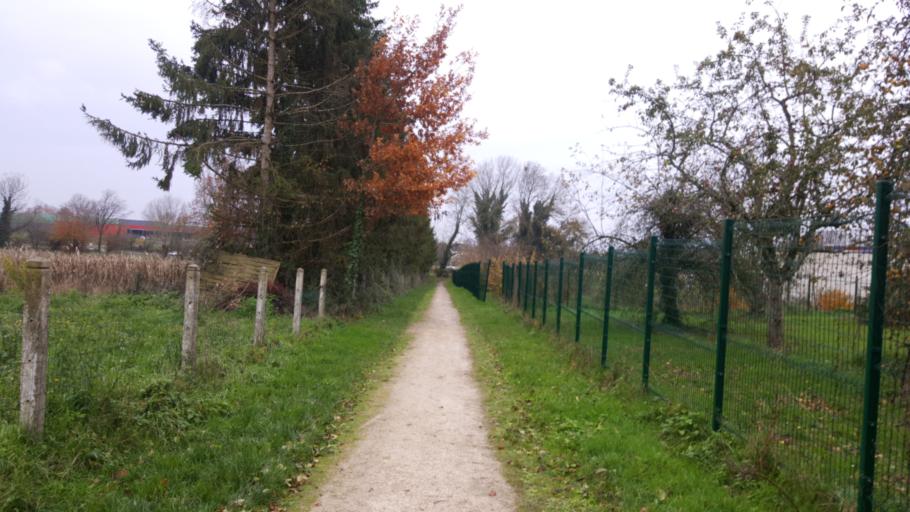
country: FR
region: Poitou-Charentes
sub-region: Departement des Deux-Sevres
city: Melle
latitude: 46.2312
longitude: -0.1302
